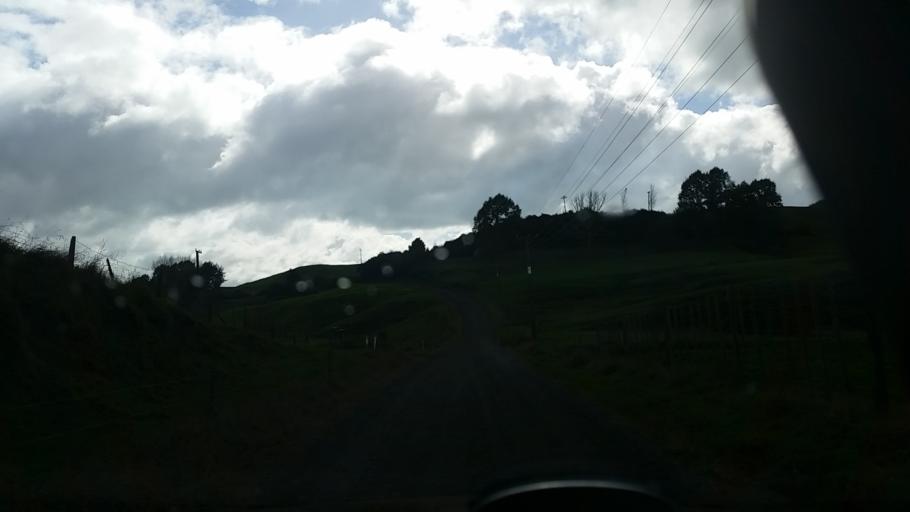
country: NZ
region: Waikato
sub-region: Matamata-Piako District
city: Matamata
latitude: -37.8118
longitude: 175.6730
